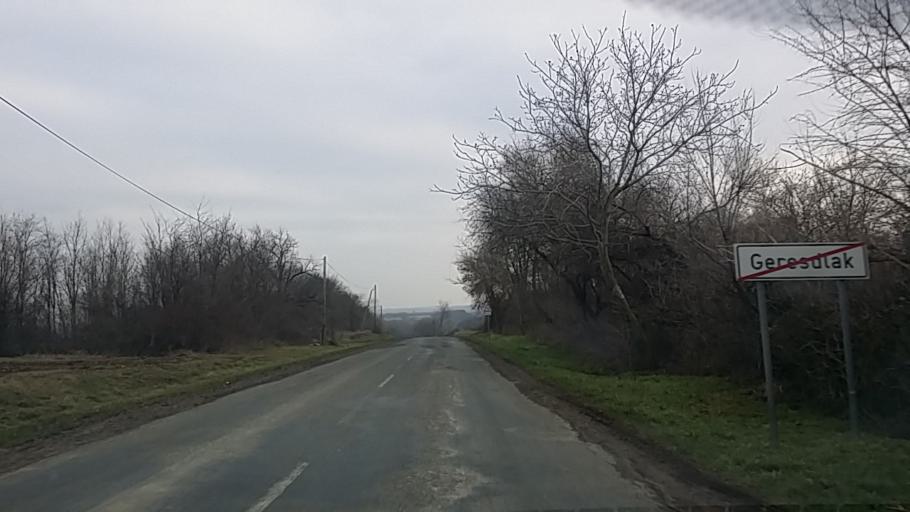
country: HU
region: Baranya
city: Pecsvarad
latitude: 46.1061
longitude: 18.5369
